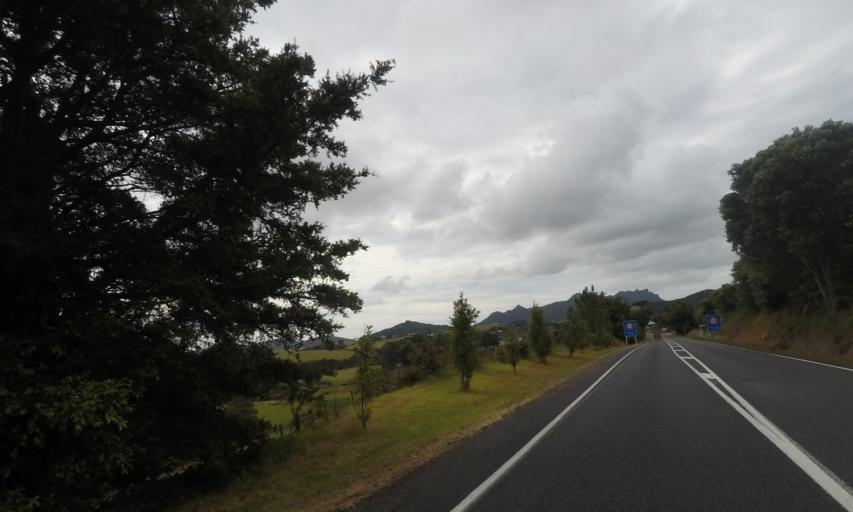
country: NZ
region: Northland
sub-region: Whangarei
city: Ruakaka
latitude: -35.7656
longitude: 174.4746
